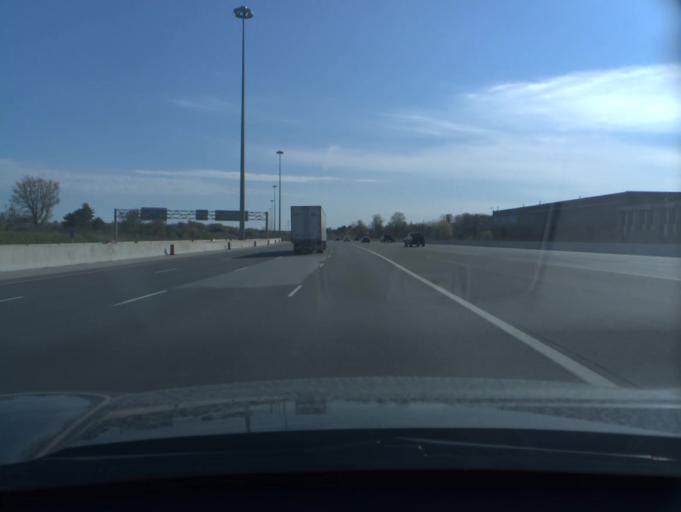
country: CA
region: Ontario
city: North Perth
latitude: 43.8114
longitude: -81.0000
